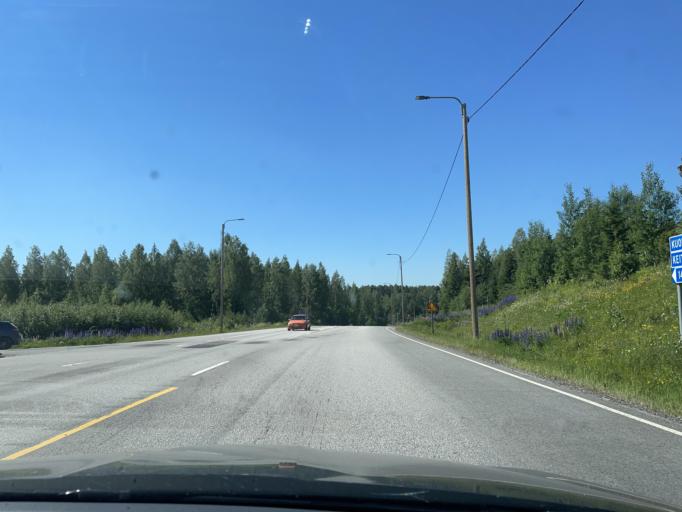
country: FI
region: Central Finland
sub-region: Saarijaervi-Viitasaari
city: Viitasaari
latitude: 63.1421
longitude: 25.8471
